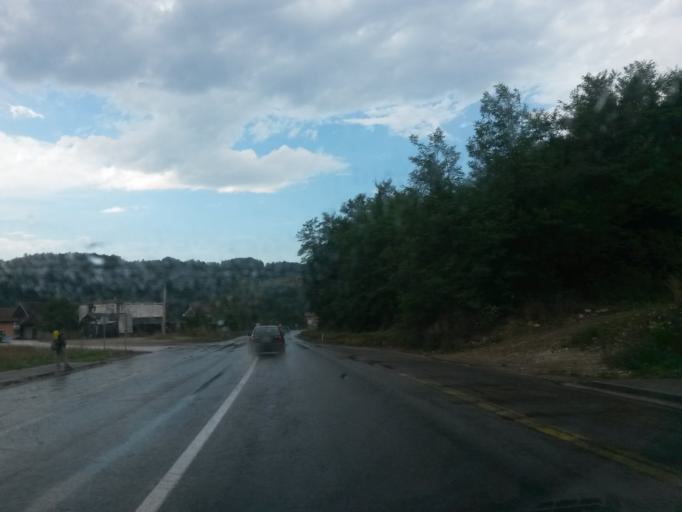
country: BA
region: Federation of Bosnia and Herzegovina
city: Lijesnica
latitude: 44.5095
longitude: 18.0819
